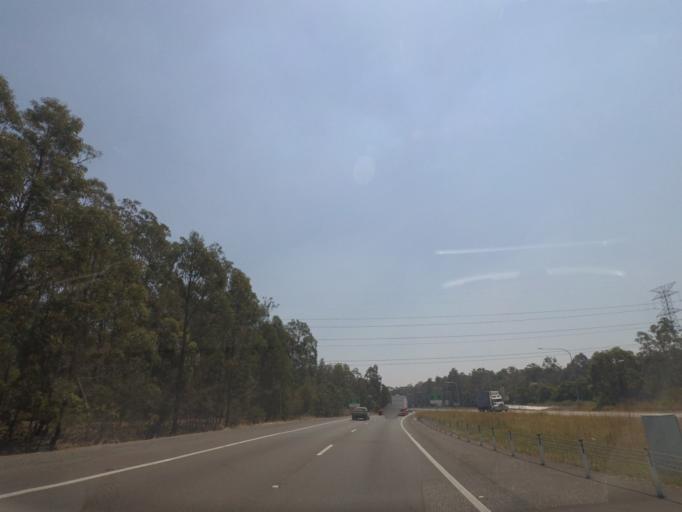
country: AU
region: New South Wales
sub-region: Newcastle
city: Beresfield
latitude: -32.8194
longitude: 151.6345
